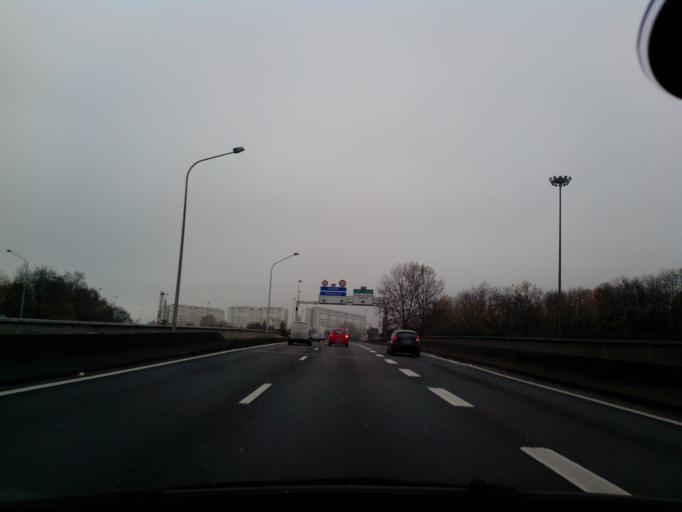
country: FR
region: Ile-de-France
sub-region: Departement du Val-de-Marne
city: Fresnes
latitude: 48.7563
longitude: 2.3351
